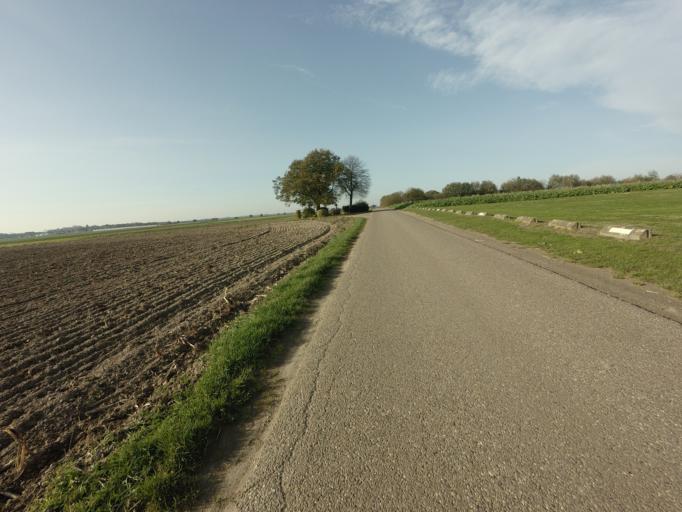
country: DE
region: North Rhine-Westphalia
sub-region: Regierungsbezirk Koln
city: Selfkant
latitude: 51.0398
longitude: 5.9333
